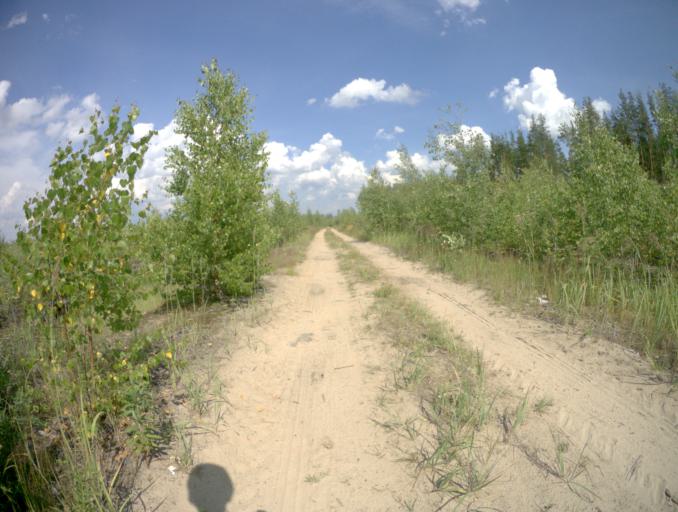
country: RU
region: Ivanovo
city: Talitsy
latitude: 56.5330
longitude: 42.2429
